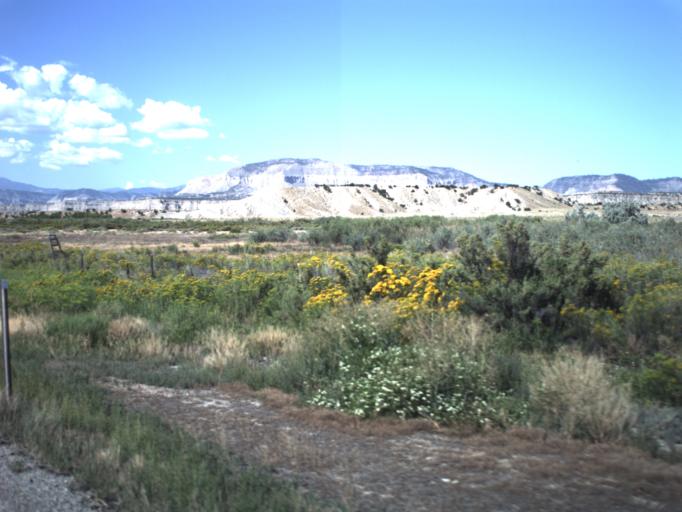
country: US
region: Utah
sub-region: Emery County
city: Ferron
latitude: 38.9096
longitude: -111.2686
